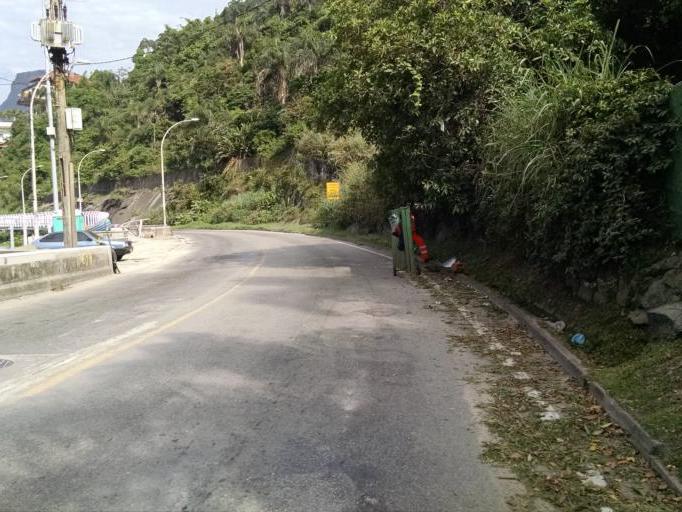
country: BR
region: Rio de Janeiro
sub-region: Rio De Janeiro
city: Rio de Janeiro
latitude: -22.9994
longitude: -43.2475
